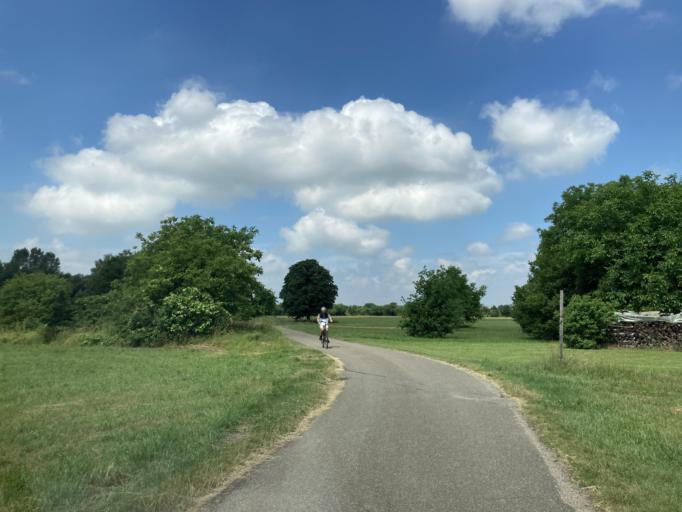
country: DE
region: Baden-Wuerttemberg
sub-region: Karlsruhe Region
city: Hambrucken
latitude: 49.1743
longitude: 8.5217
